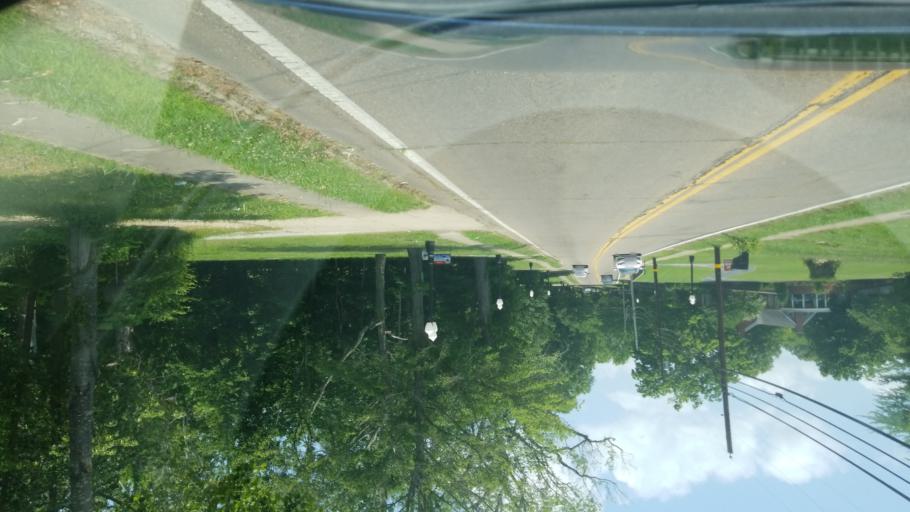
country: US
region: Tennessee
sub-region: Carroll County
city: Huntingdon
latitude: 36.0027
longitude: -88.4216
